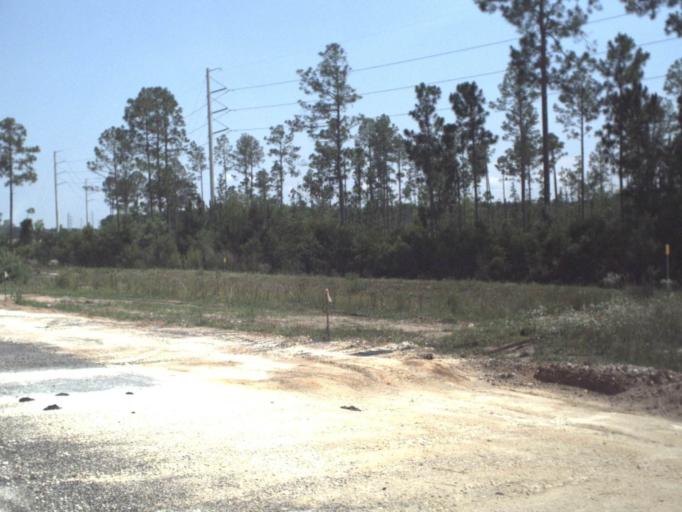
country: US
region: Florida
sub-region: Clay County
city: Bellair-Meadowbrook Terrace
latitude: 30.2535
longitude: -81.8518
